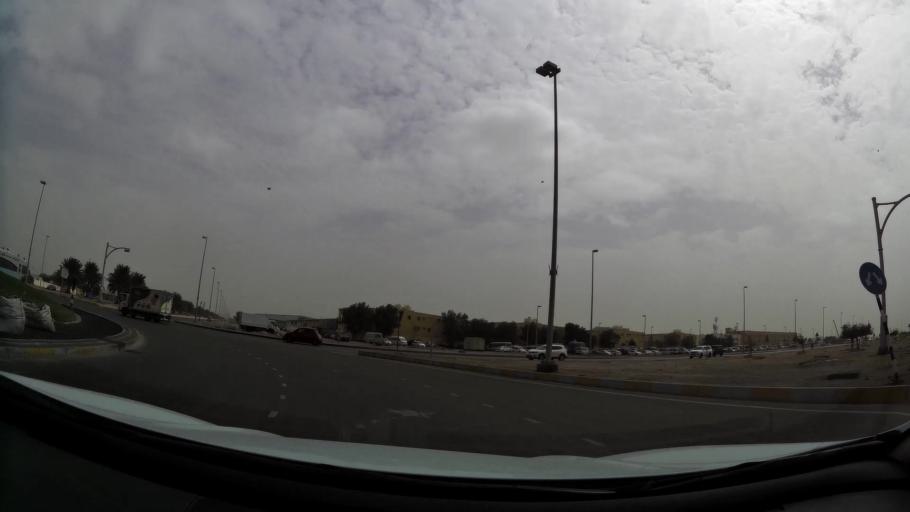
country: AE
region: Abu Dhabi
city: Abu Dhabi
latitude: 24.3714
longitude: 54.4716
